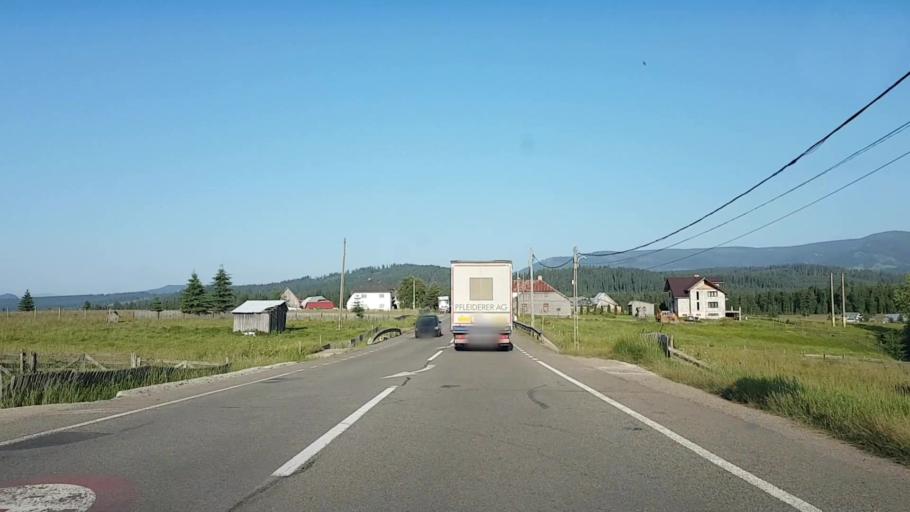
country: RO
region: Suceava
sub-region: Comuna Poiana Stampei
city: Poiana Stampei
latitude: 47.3004
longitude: 25.1019
